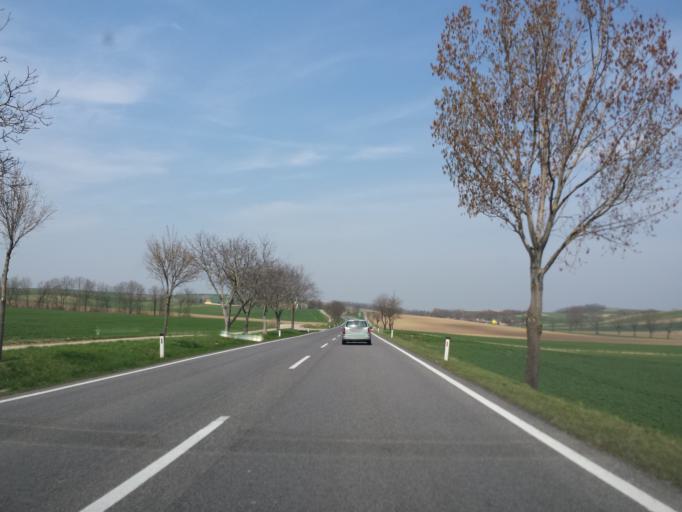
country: AT
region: Lower Austria
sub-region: Politischer Bezirk Mistelbach
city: Wilfersdorf
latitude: 48.6145
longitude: 16.6480
